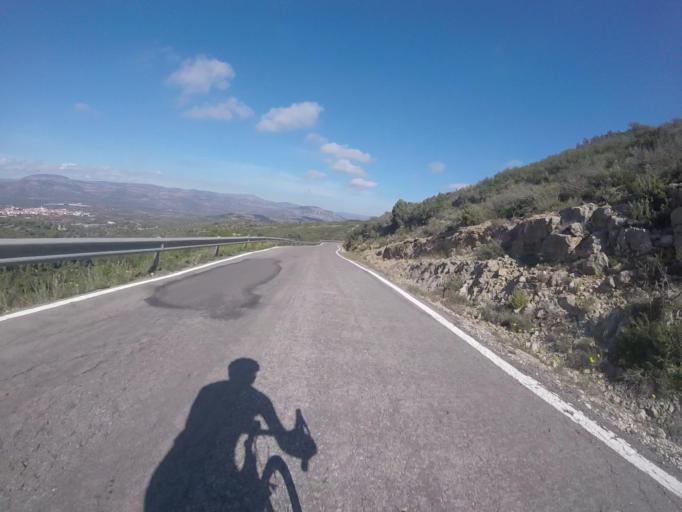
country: ES
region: Valencia
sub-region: Provincia de Castello
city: Albocasser
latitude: 40.3481
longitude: 0.0495
